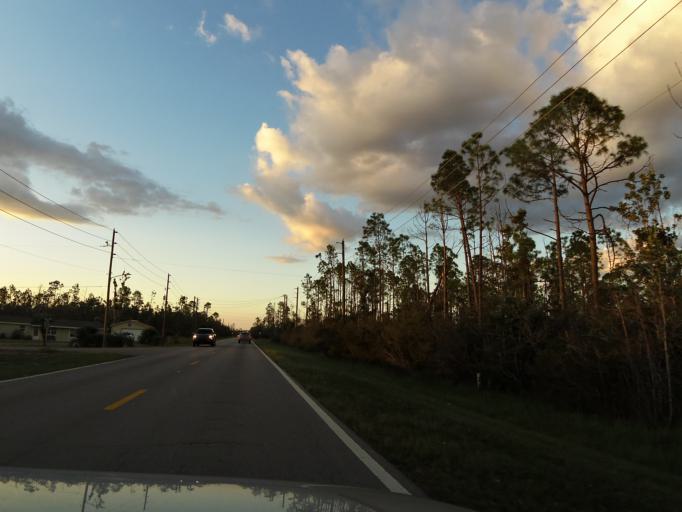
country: US
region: Florida
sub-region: Bay County
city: Mexico Beach
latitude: 29.9306
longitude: -85.3885
